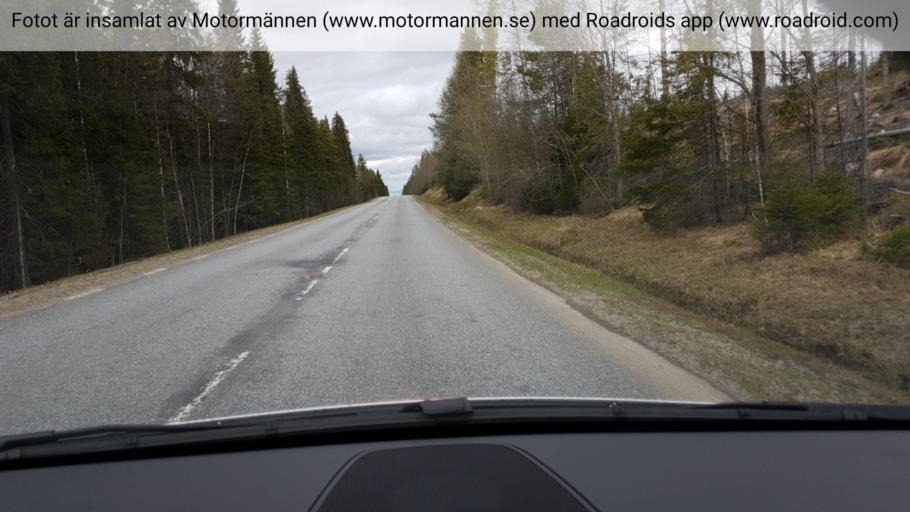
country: SE
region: Jaemtland
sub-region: Braecke Kommun
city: Braecke
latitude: 62.7981
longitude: 15.4675
